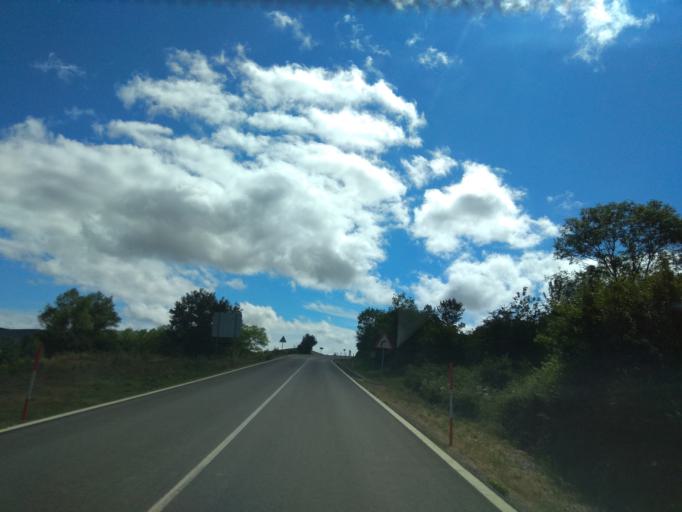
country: ES
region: Cantabria
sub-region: Provincia de Cantabria
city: Villaescusa
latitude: 42.9599
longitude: -4.1657
